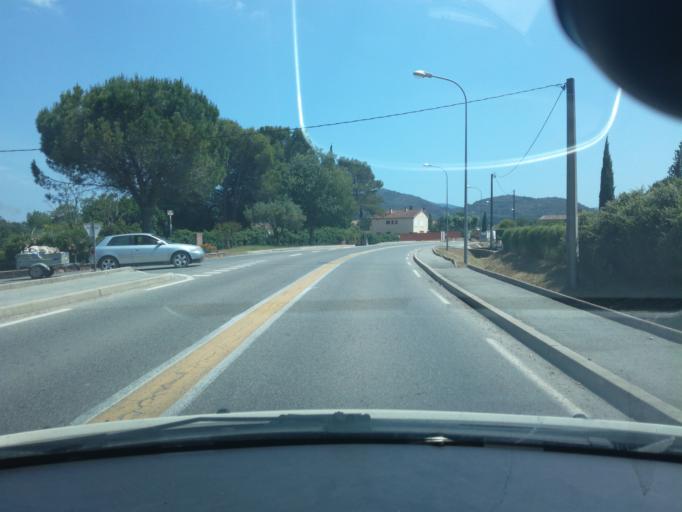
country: FR
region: Provence-Alpes-Cote d'Azur
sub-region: Departement du Var
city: Le Muy
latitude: 43.4788
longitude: 6.5662
